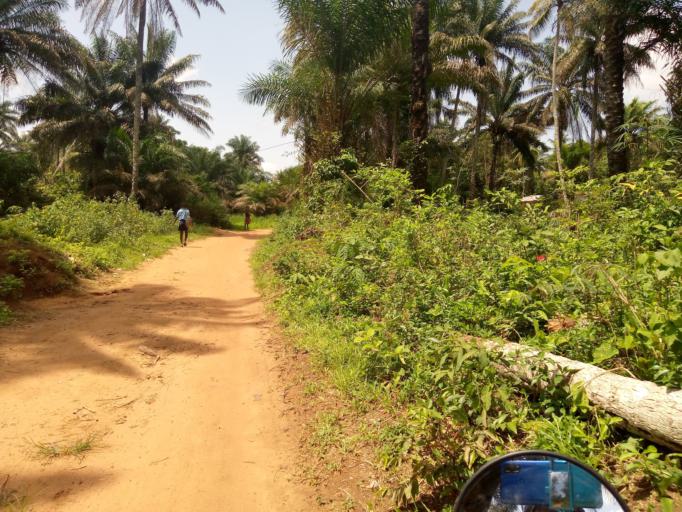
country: SL
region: Western Area
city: Waterloo
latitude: 8.3589
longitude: -12.9261
